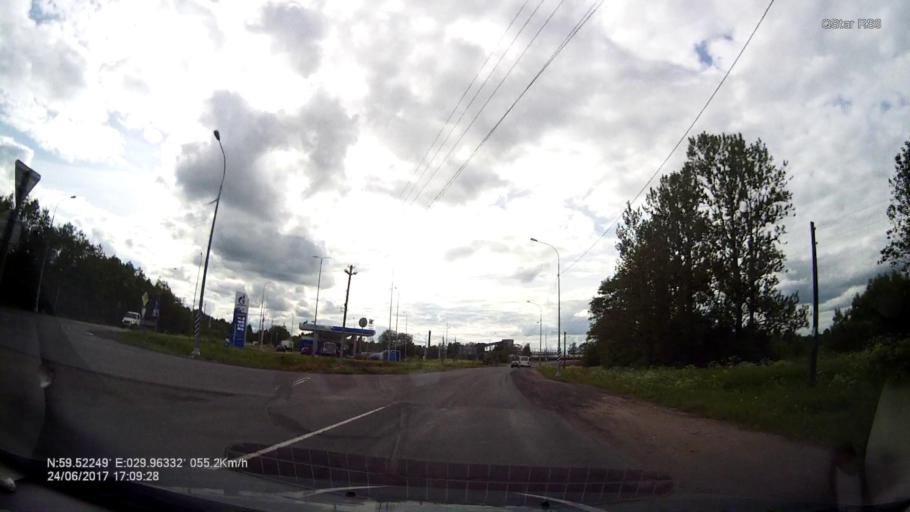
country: RU
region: Leningrad
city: Voyskovitsy
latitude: 59.5226
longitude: 29.9628
